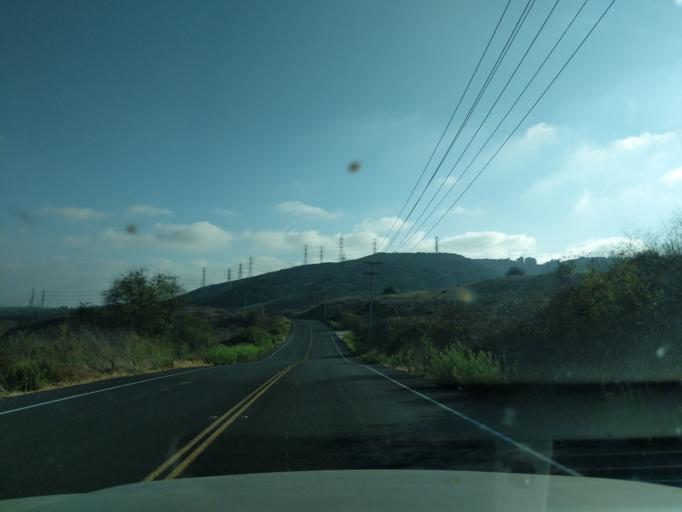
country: US
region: California
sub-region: Orange County
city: San Clemente
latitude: 33.4211
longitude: -117.5770
